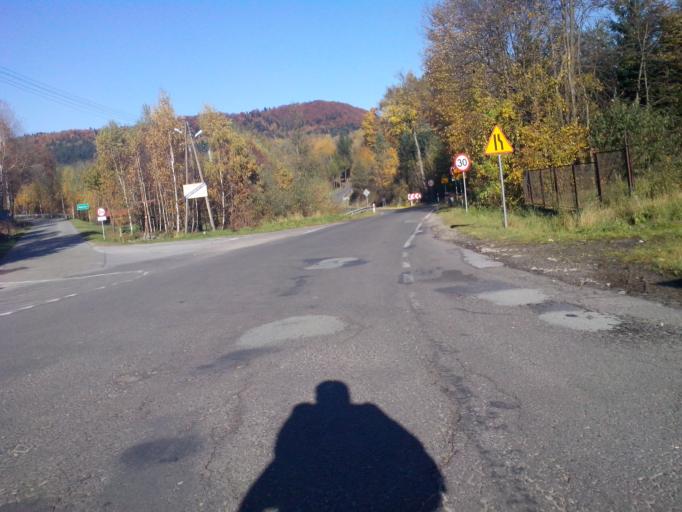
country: PL
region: Subcarpathian Voivodeship
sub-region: Powiat krosnienski
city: Korczyna
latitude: 49.7646
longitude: 21.7988
